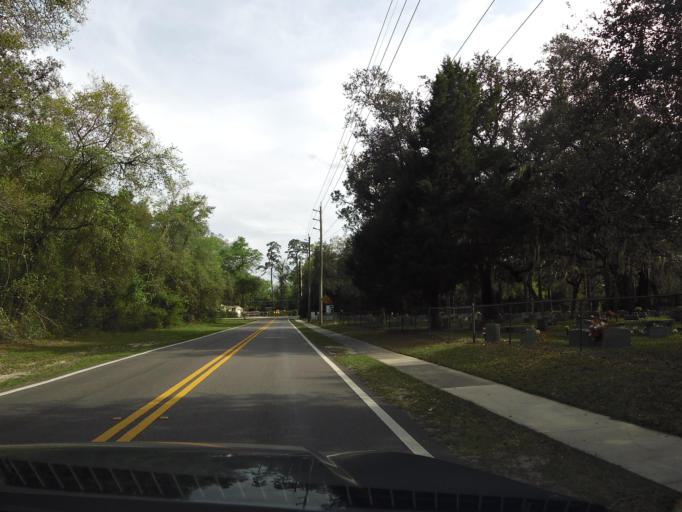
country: US
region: Florida
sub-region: Duval County
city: Jacksonville
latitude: 30.2942
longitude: -81.7651
